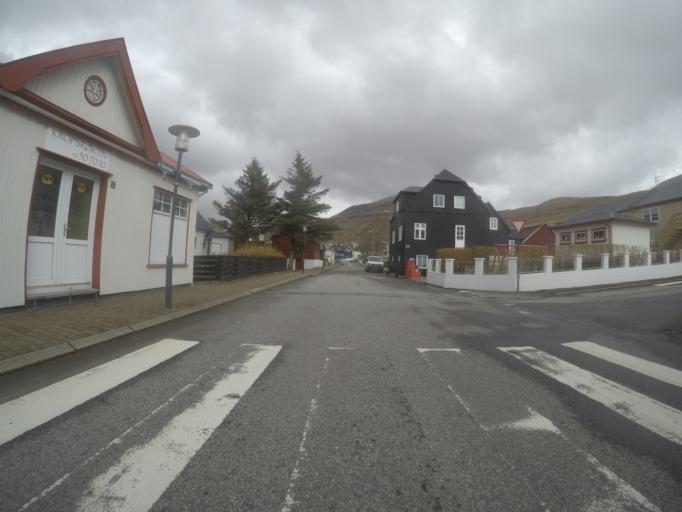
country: FO
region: Vagar
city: Midvagur
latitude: 62.0540
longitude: -7.1496
